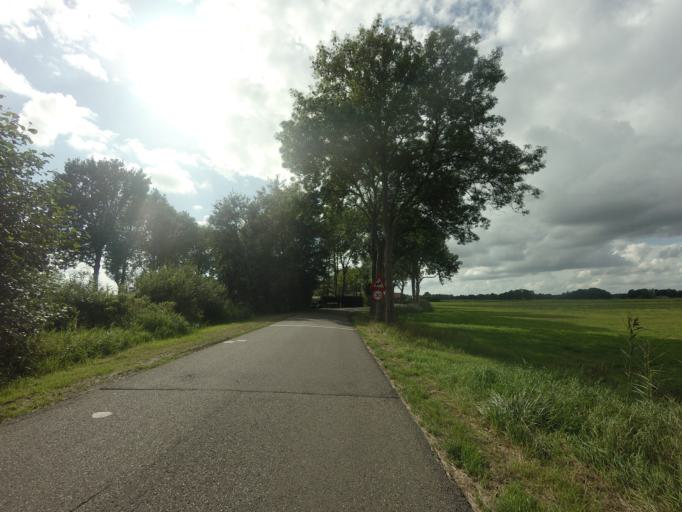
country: NL
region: Overijssel
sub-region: Gemeente Steenwijkerland
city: Giethoorn
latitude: 52.7218
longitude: 6.0624
